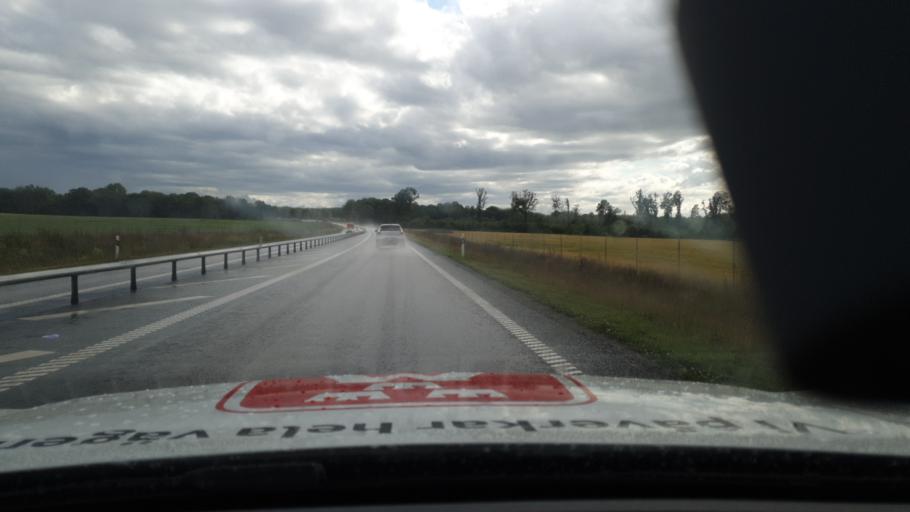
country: SE
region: Vaestra Goetaland
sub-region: Gotene Kommun
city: Kallby
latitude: 58.4905
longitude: 13.2862
